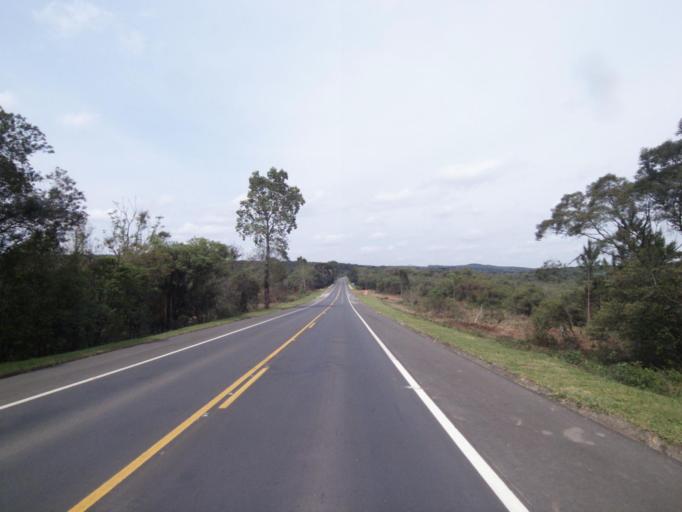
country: BR
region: Parana
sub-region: Irati
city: Irati
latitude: -25.4664
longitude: -50.5323
